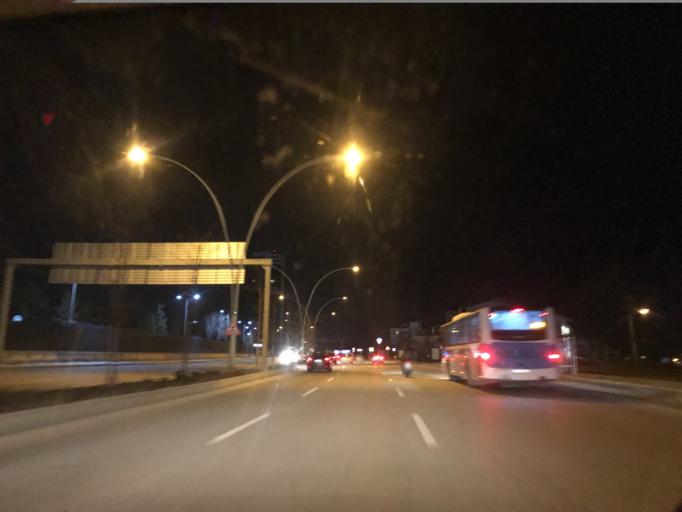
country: TR
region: Ankara
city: Cankaya
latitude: 39.8583
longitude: 32.8527
